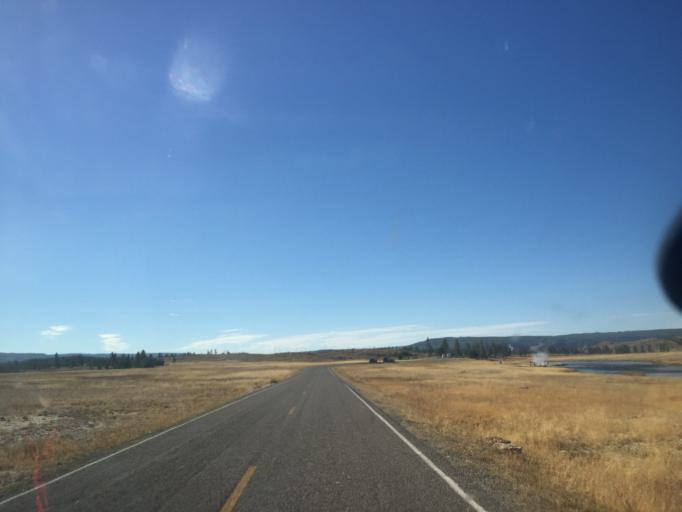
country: US
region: Montana
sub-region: Gallatin County
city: West Yellowstone
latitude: 44.5736
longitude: -110.8321
